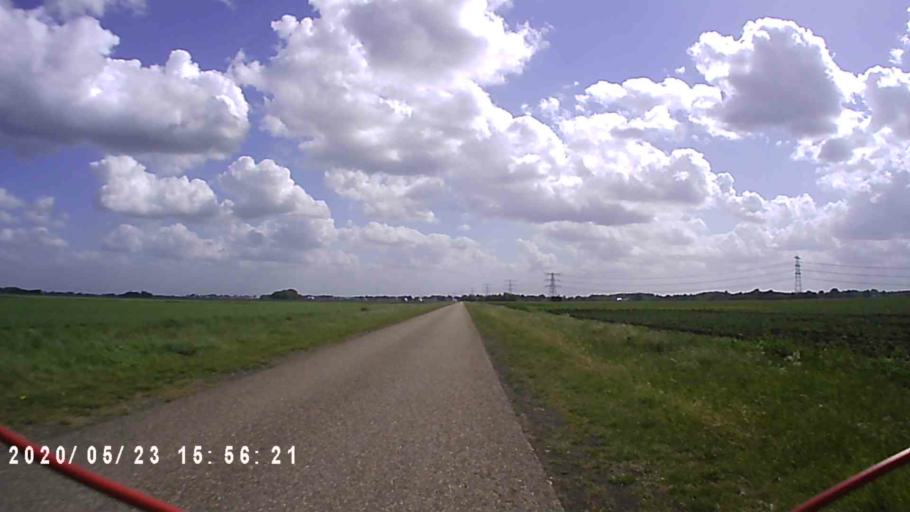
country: NL
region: Groningen
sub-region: Gemeente Delfzijl
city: Delfzijl
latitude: 53.2607
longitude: 6.9003
